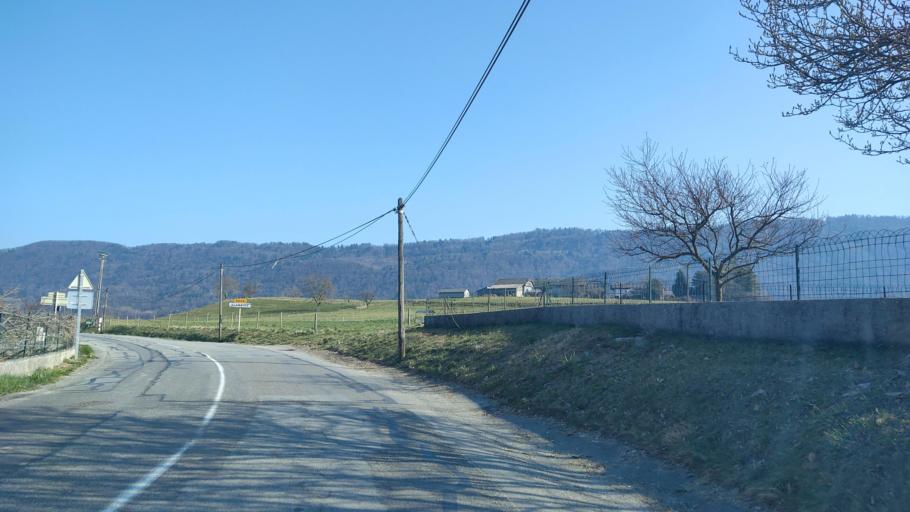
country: FR
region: Rhone-Alpes
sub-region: Departement de la Savoie
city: Cruet
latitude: 45.5038
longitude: 6.0965
